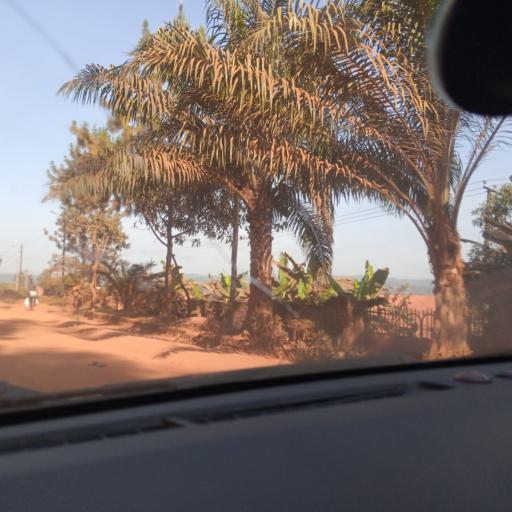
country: UG
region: Central Region
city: Masaka
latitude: -0.3348
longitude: 31.7333
